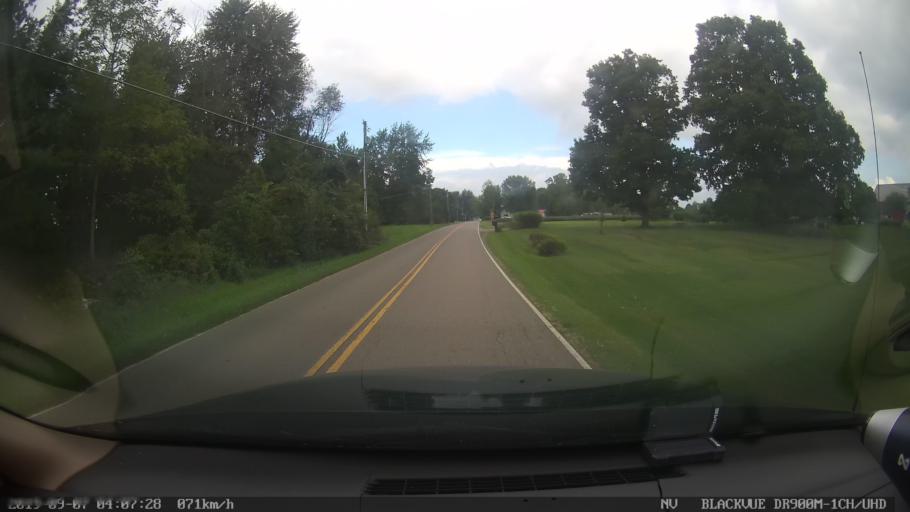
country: US
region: Ohio
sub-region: Licking County
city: Johnstown
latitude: 40.2067
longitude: -82.6140
